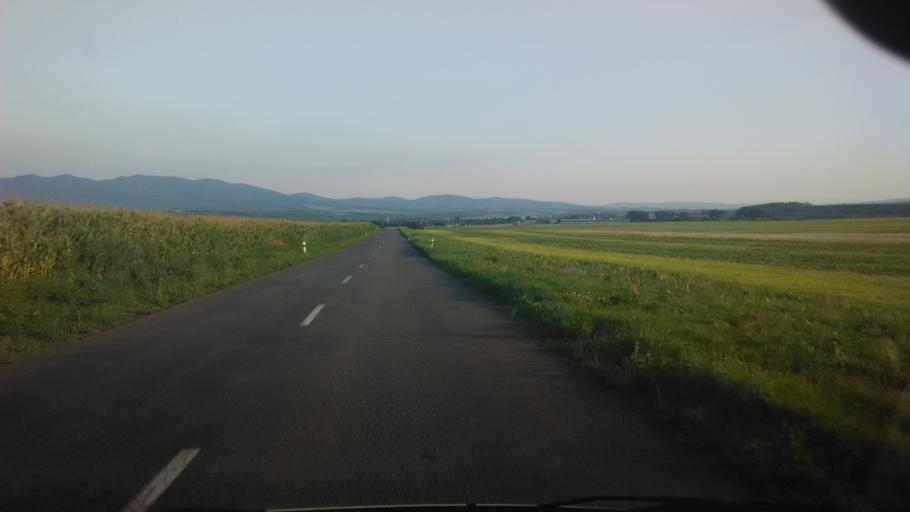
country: SK
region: Nitriansky
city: Zeliezovce
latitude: 48.0444
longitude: 18.7998
